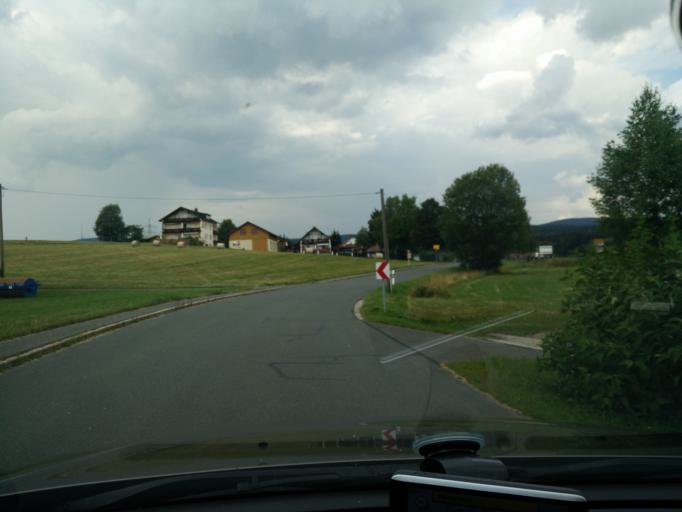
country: DE
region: Bavaria
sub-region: Upper Franconia
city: Fichtelberg
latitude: 49.9844
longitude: 11.8582
